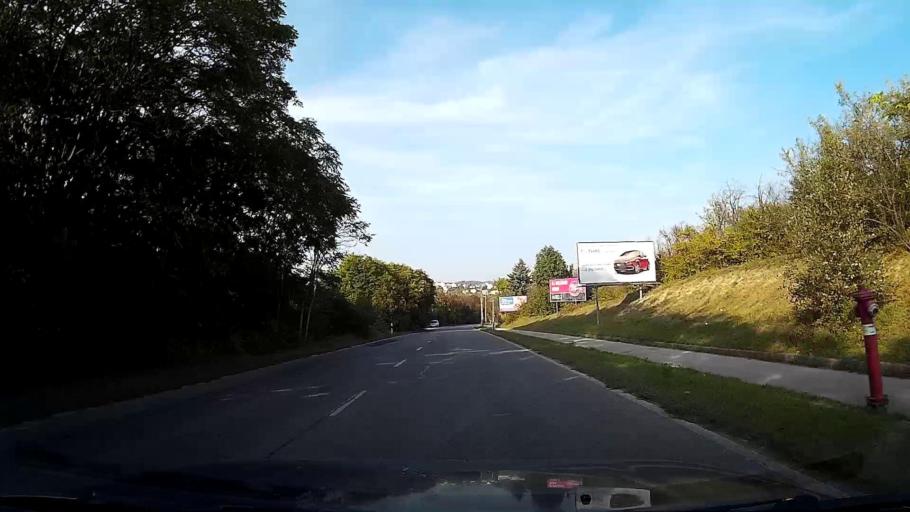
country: HU
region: Pest
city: Budaors
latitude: 47.4534
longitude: 18.9915
